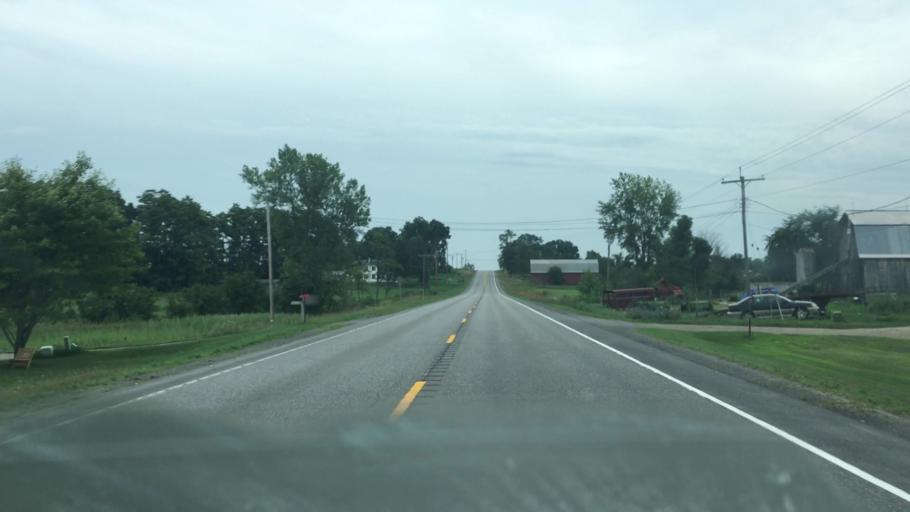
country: US
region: New York
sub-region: Clinton County
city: Morrisonville
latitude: 44.6472
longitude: -73.5680
